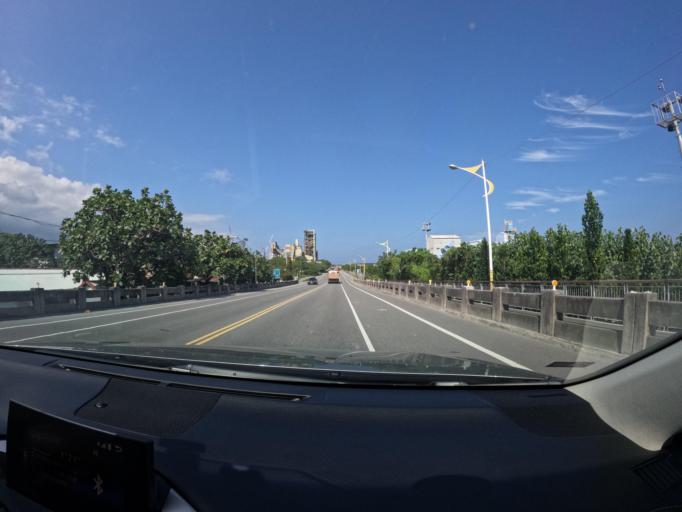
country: TW
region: Taiwan
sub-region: Hualien
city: Hualian
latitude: 24.0042
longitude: 121.6353
